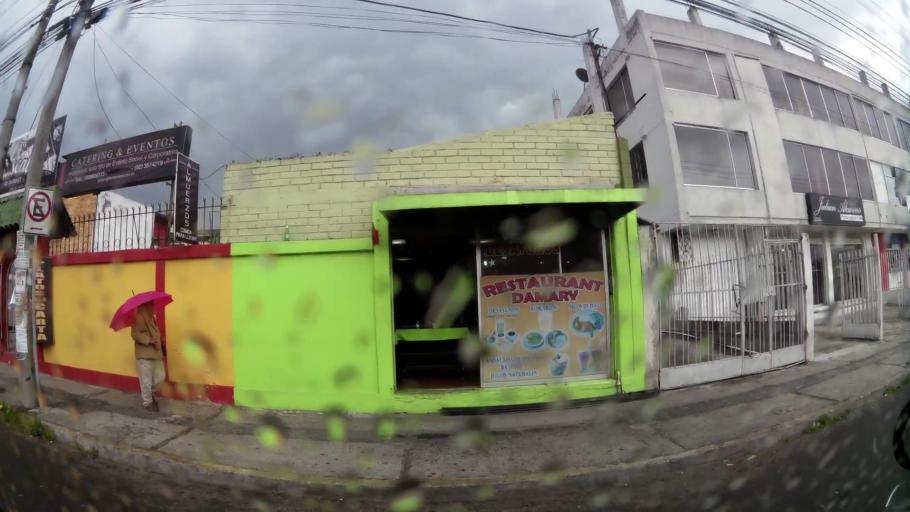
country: EC
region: Pichincha
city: Quito
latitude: -0.1047
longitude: -78.4913
